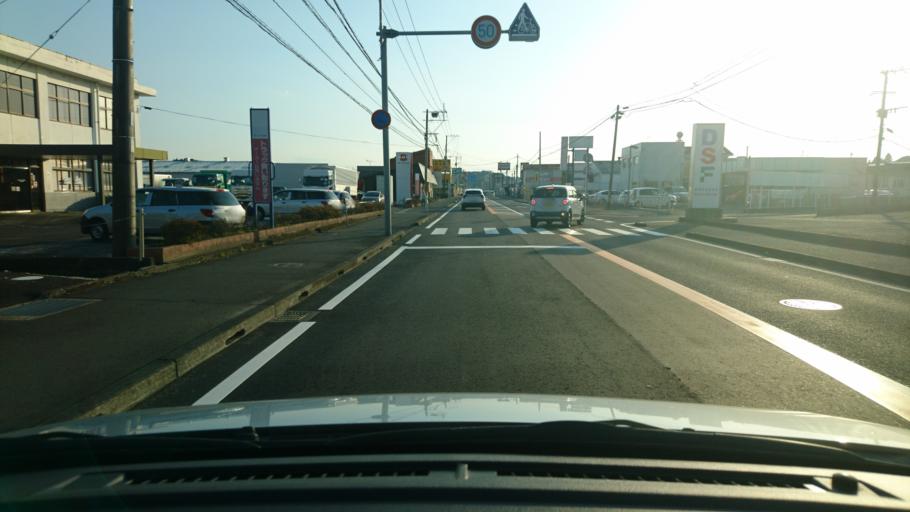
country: JP
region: Miyazaki
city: Miyazaki-shi
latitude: 31.9799
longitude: 131.4456
